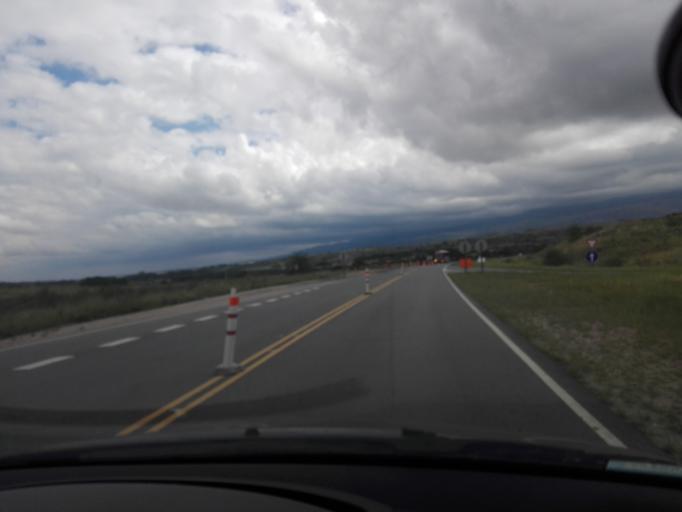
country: AR
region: Cordoba
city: Cuesta Blanca
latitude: -31.5711
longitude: -64.5887
